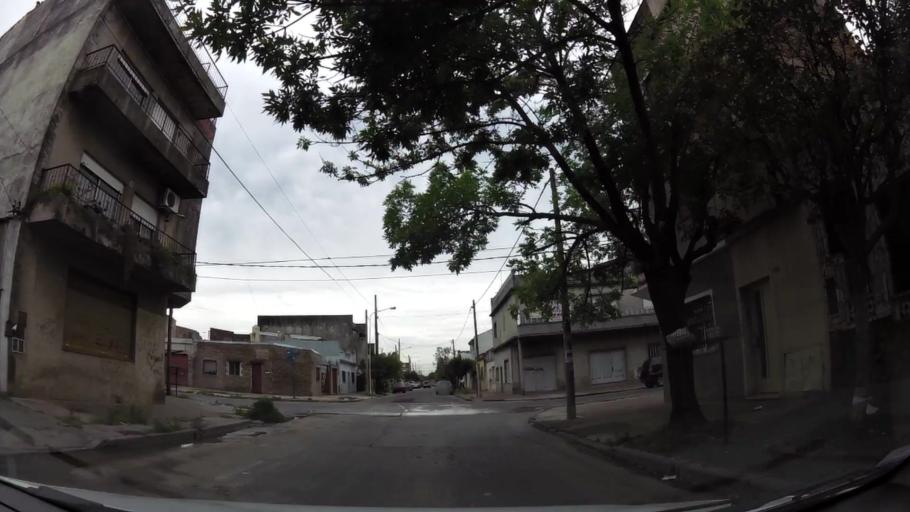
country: AR
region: Buenos Aires F.D.
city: Villa Lugano
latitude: -34.6761
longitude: -58.5141
